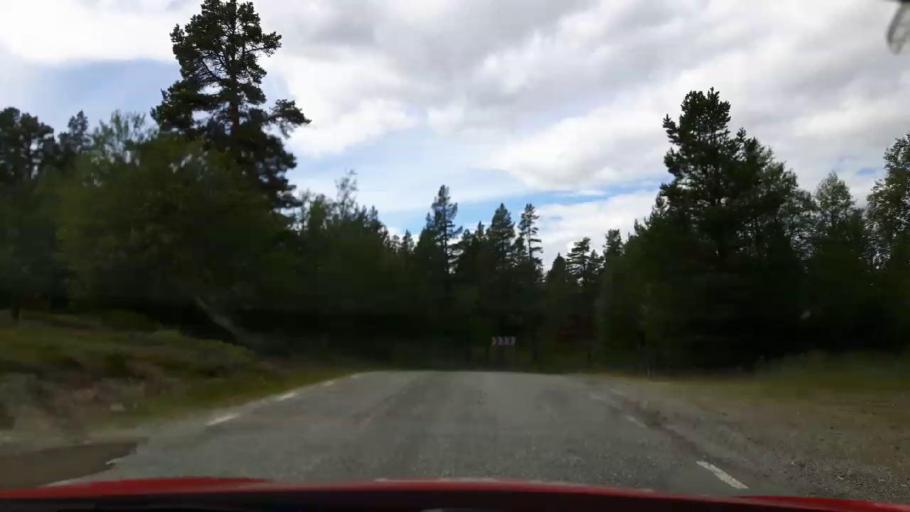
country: NO
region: Hedmark
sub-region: Engerdal
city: Engerdal
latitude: 62.2855
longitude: 12.8380
